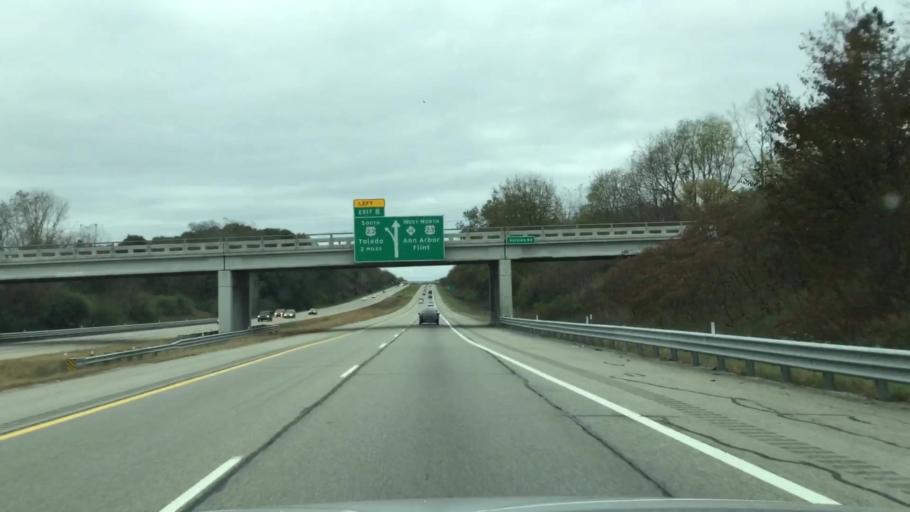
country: US
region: Michigan
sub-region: Washtenaw County
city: Ypsilanti
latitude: 42.3259
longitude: -83.6447
